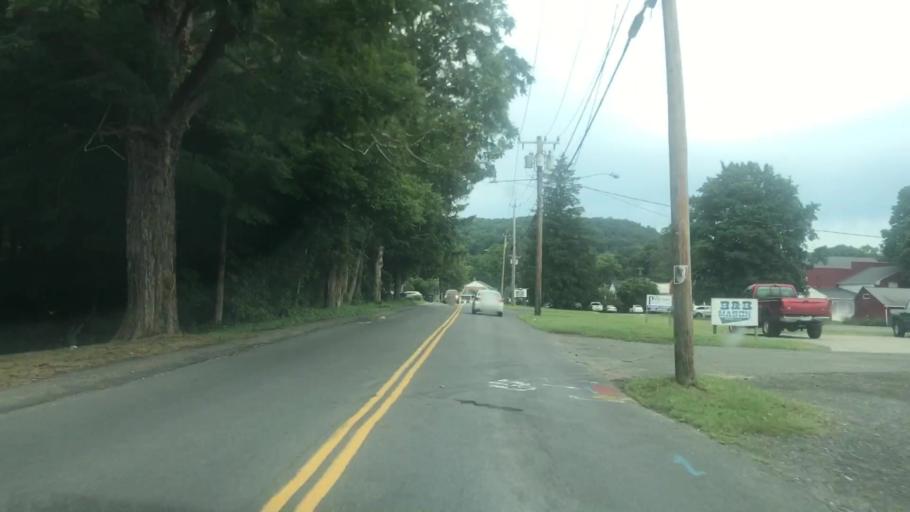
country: US
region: Connecticut
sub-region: Litchfield County
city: New Milford
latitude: 41.5830
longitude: -73.4215
